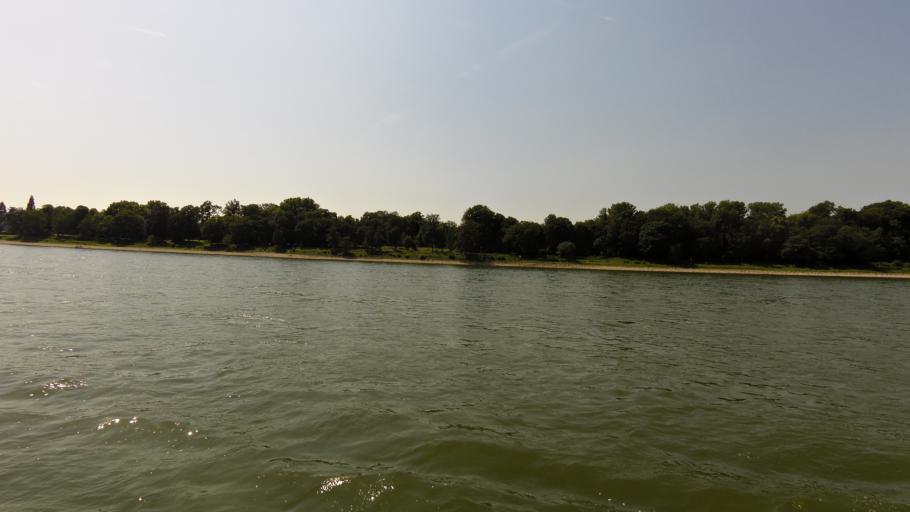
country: DE
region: North Rhine-Westphalia
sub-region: Regierungsbezirk Koln
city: Konigswinter
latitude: 50.6757
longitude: 7.1884
